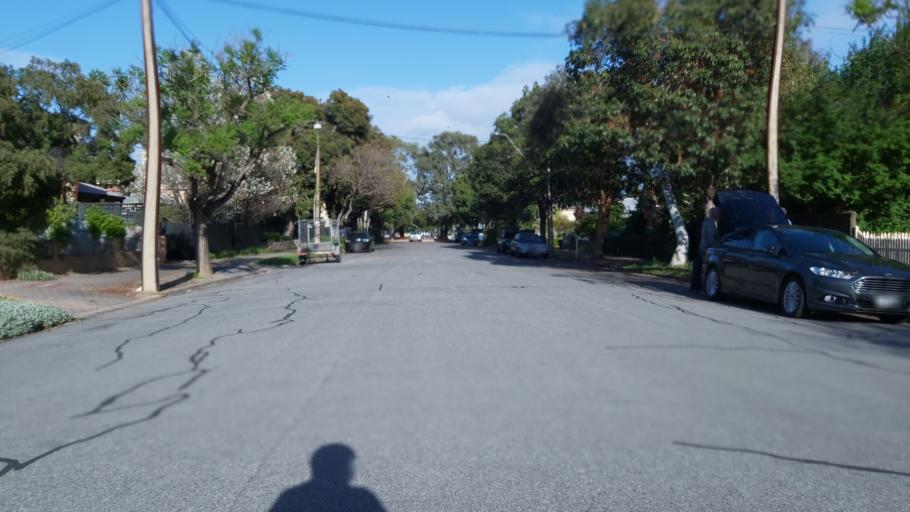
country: AU
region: South Australia
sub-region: Unley
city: Fullarton
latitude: -34.9490
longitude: 138.6156
